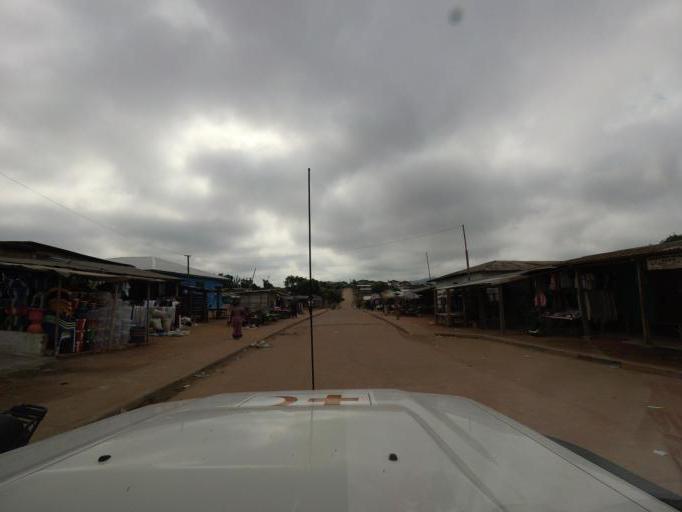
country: LR
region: Lofa
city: Voinjama
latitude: 8.4242
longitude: -9.7543
